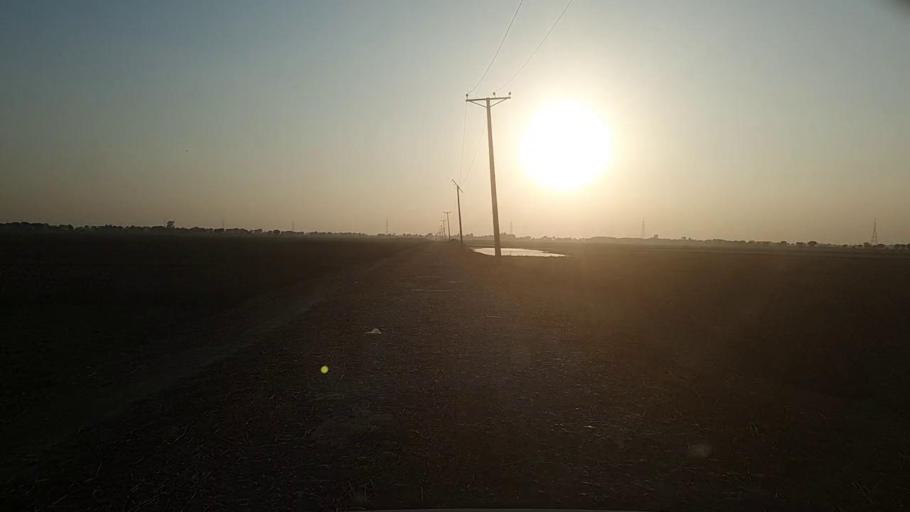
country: PK
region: Sindh
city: Mehar
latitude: 27.1957
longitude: 67.7521
